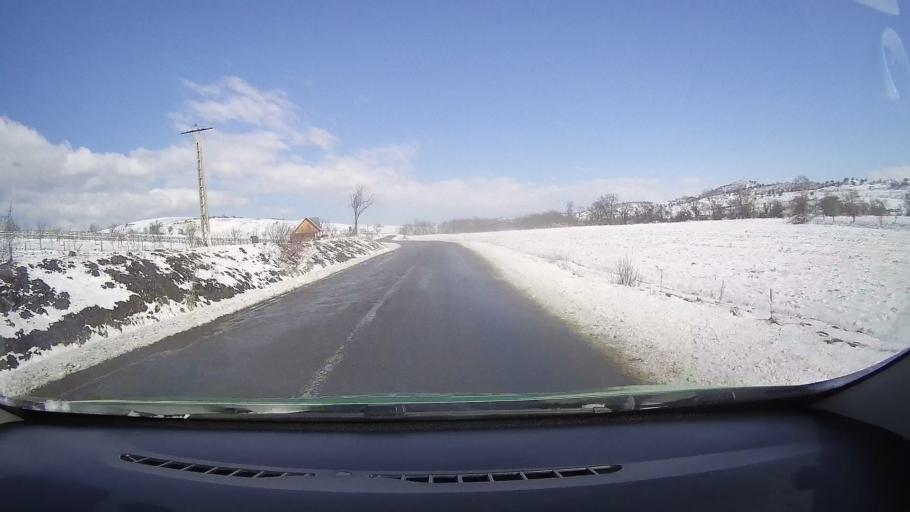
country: RO
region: Sibiu
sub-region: Comuna Vurpar
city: Vurpar
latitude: 45.8757
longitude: 24.3199
